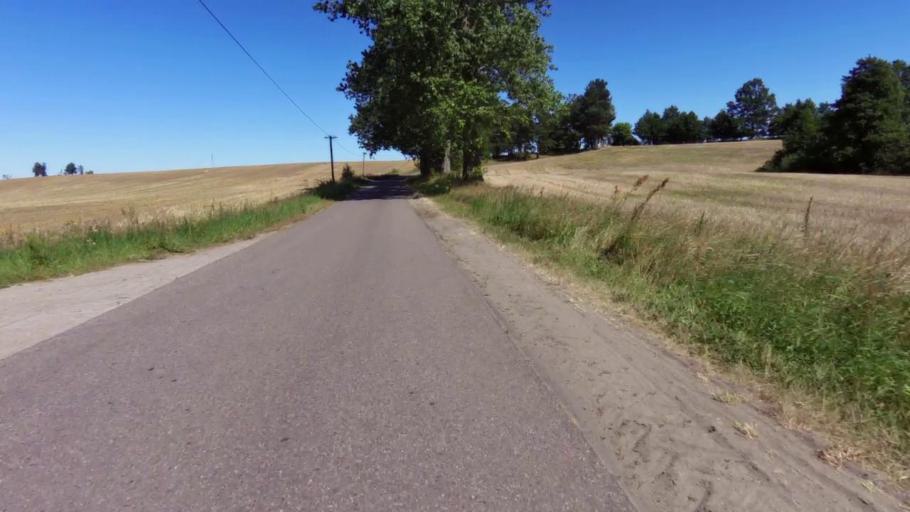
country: PL
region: West Pomeranian Voivodeship
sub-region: Powiat drawski
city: Czaplinek
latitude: 53.5438
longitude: 16.2093
